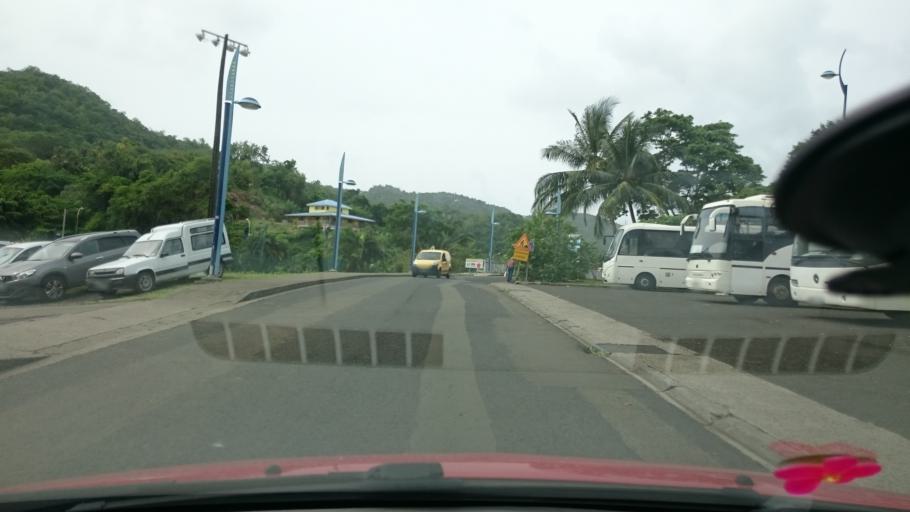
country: MQ
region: Martinique
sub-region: Martinique
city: Riviere-Pilote
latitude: 14.4859
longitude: -60.9041
